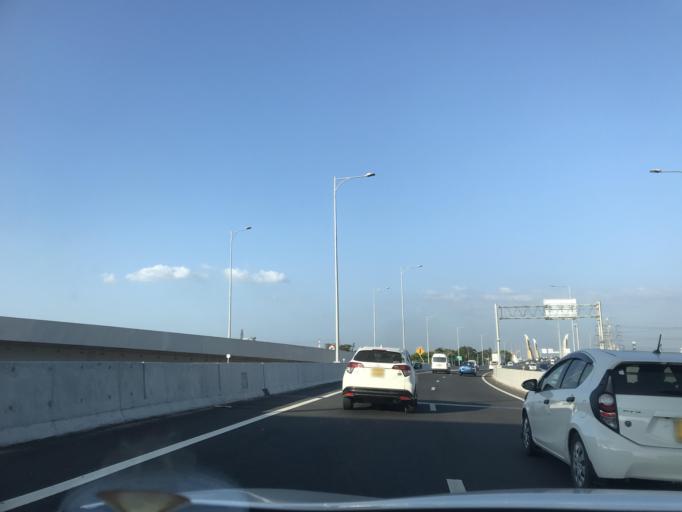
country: LK
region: Western
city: Kolonnawa
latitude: 6.9501
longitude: 79.8788
